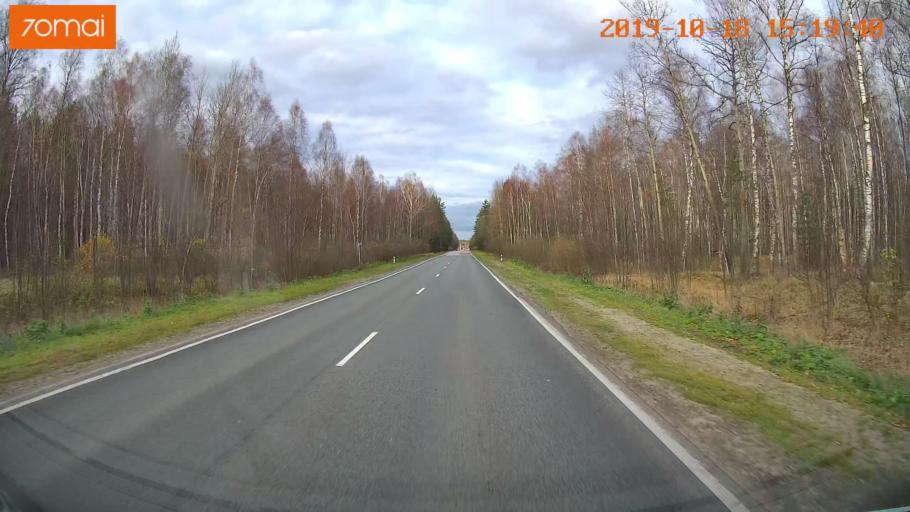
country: RU
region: Vladimir
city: Anopino
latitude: 55.6764
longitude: 40.7393
